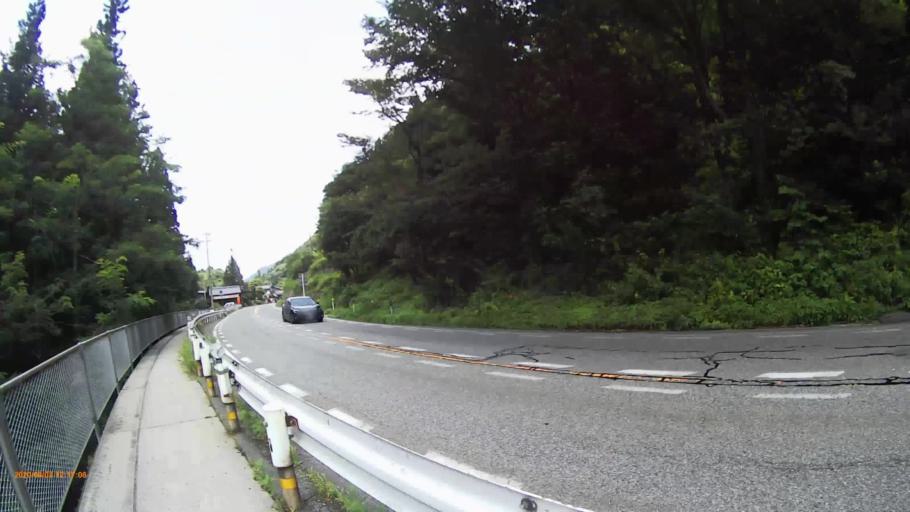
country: JP
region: Nagano
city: Shiojiri
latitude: 36.0337
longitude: 137.8797
